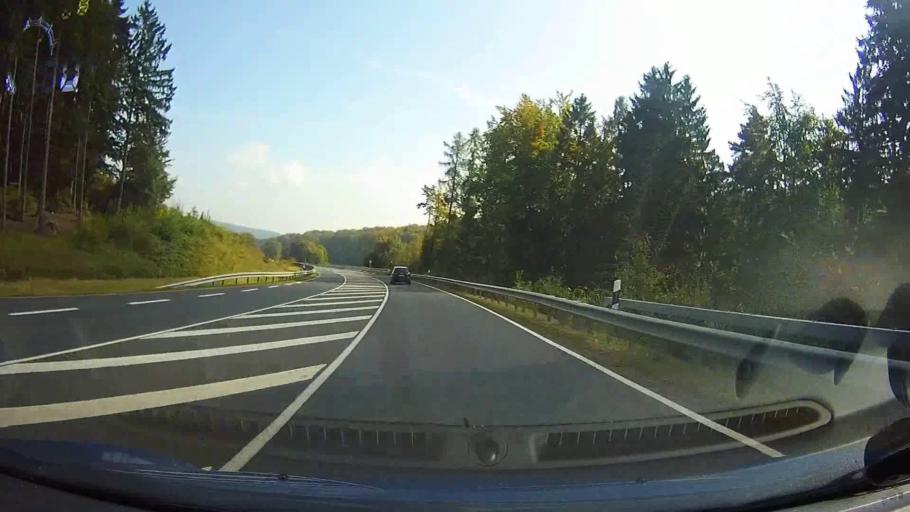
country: DE
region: Lower Saxony
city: Adelebsen
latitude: 51.6361
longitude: 9.7661
